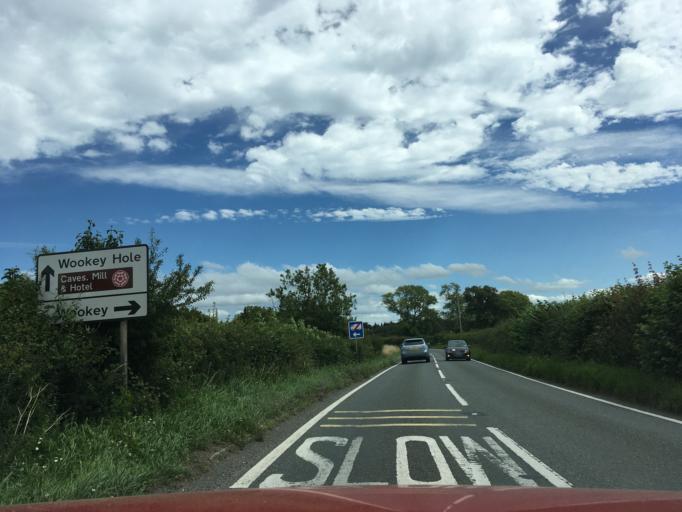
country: GB
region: England
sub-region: Somerset
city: Wells
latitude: 51.2145
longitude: -2.6789
